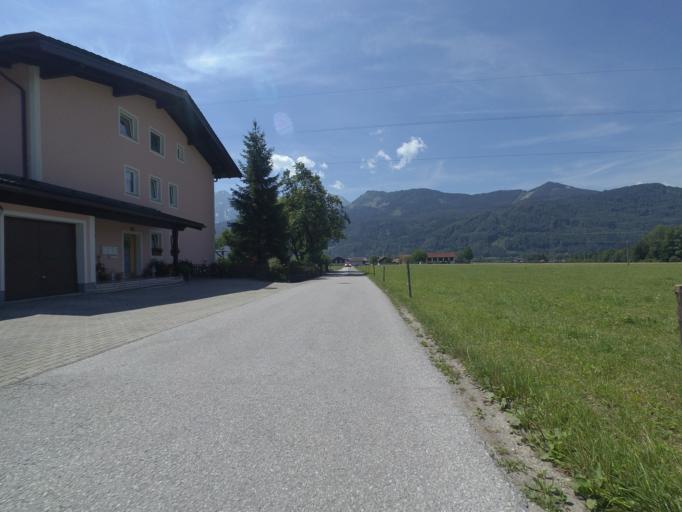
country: AT
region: Salzburg
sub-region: Politischer Bezirk Hallein
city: Kuchl
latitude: 47.6542
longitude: 13.1447
